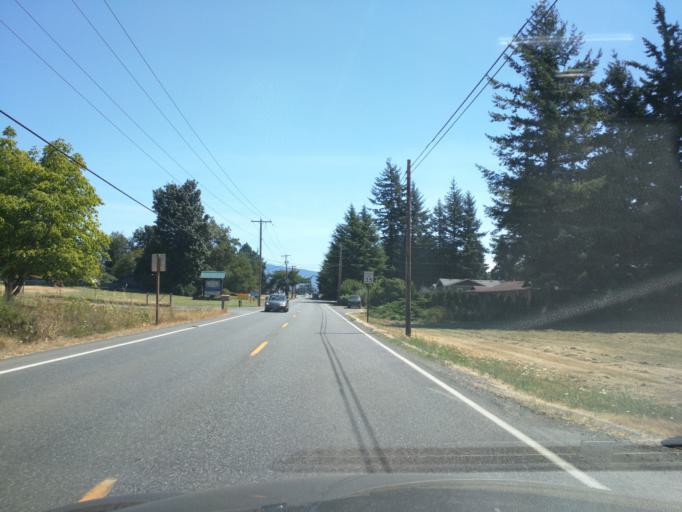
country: US
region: Washington
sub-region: Whatcom County
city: Lynden
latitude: 48.8917
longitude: -122.4490
